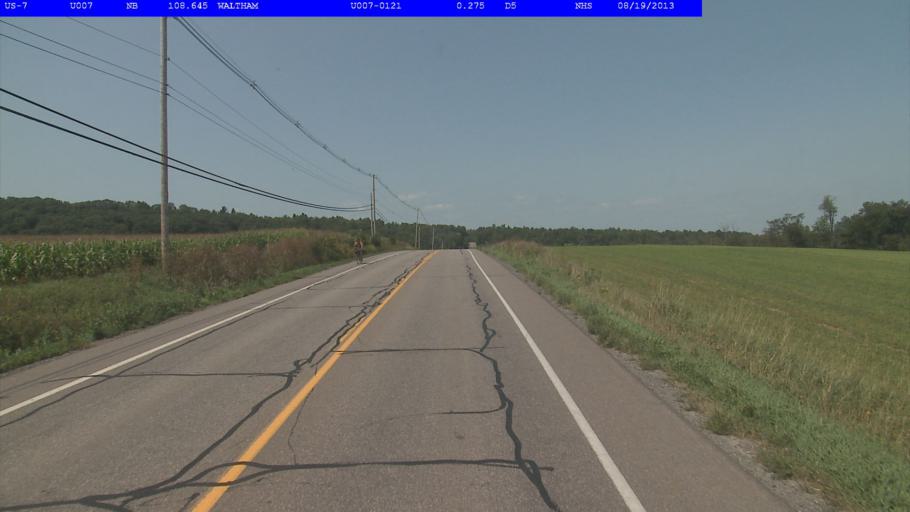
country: US
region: Vermont
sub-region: Addison County
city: Vergennes
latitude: 44.1506
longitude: -73.2139
